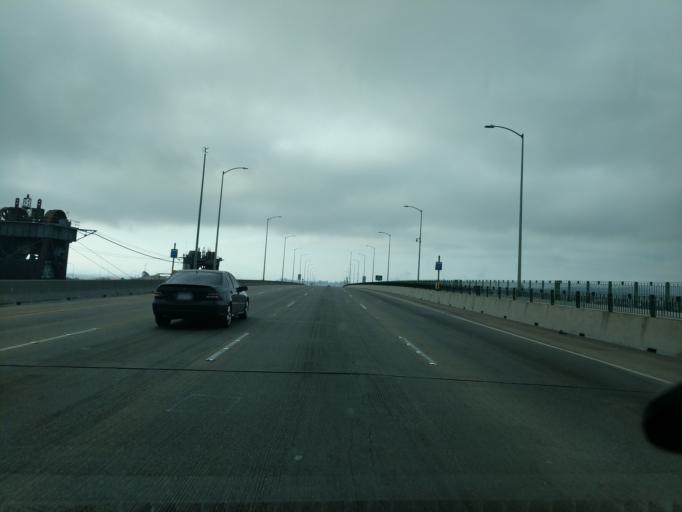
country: US
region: California
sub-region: Contra Costa County
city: Martinez
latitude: 38.0396
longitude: -122.1223
